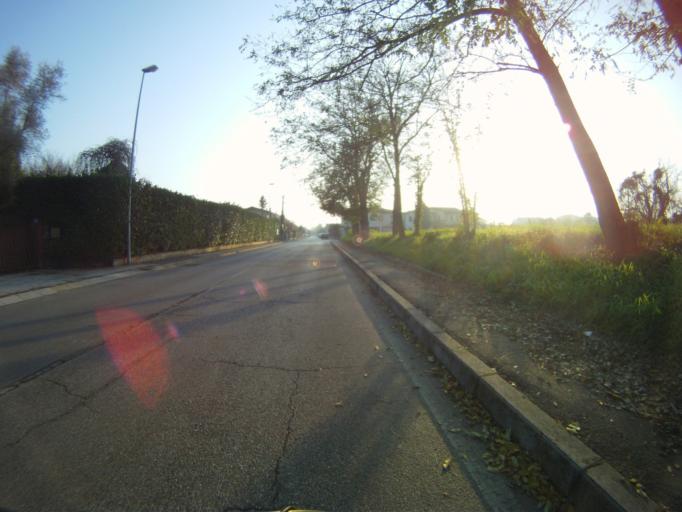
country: IT
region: Veneto
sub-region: Provincia di Padova
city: Ponte San Nicolo
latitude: 45.3783
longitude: 11.8954
